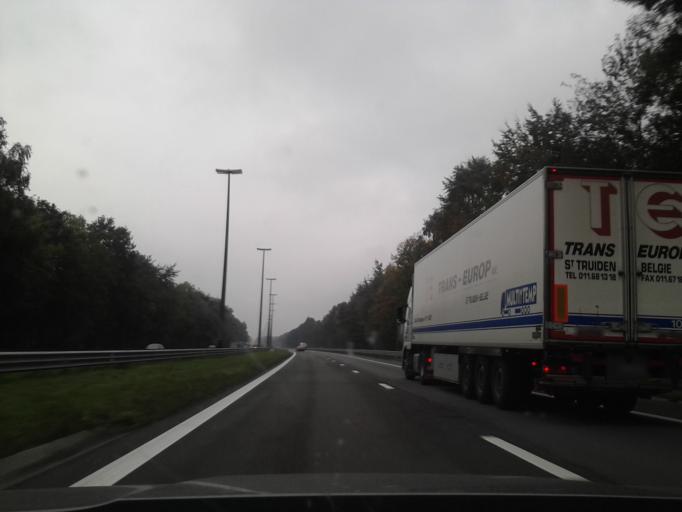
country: BE
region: Wallonia
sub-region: Province du Hainaut
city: Manage
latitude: 50.5367
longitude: 4.2211
